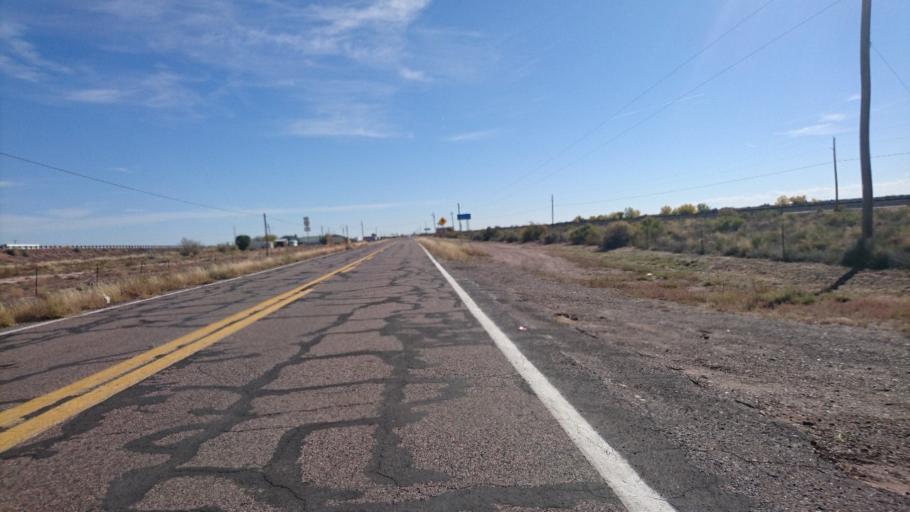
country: US
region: Arizona
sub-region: Navajo County
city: Joseph City
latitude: 34.9683
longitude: -110.4336
